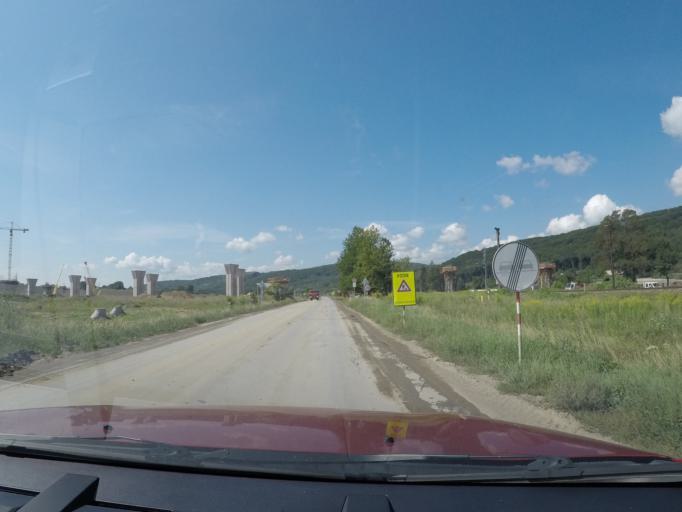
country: SK
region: Presovsky
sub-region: Okres Presov
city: Presov
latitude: 48.9651
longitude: 21.2470
